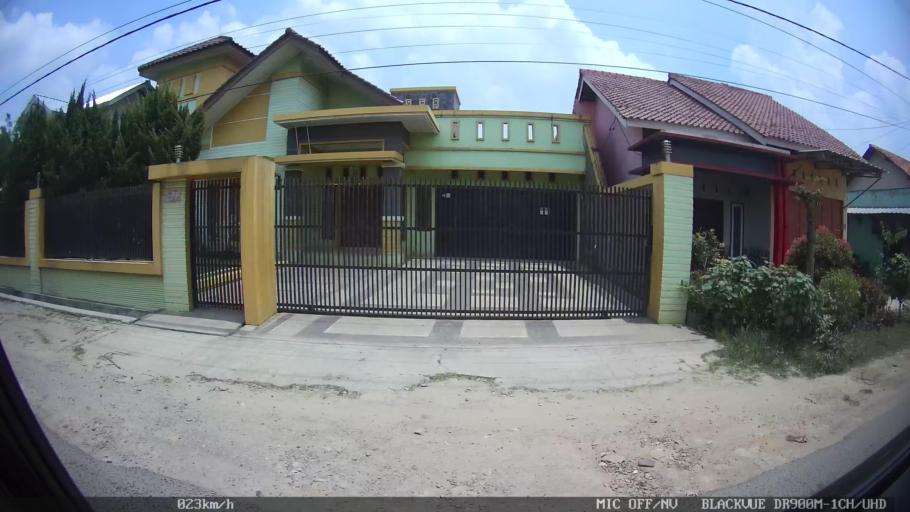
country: ID
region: Lampung
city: Pringsewu
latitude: -5.3503
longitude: 104.9799
